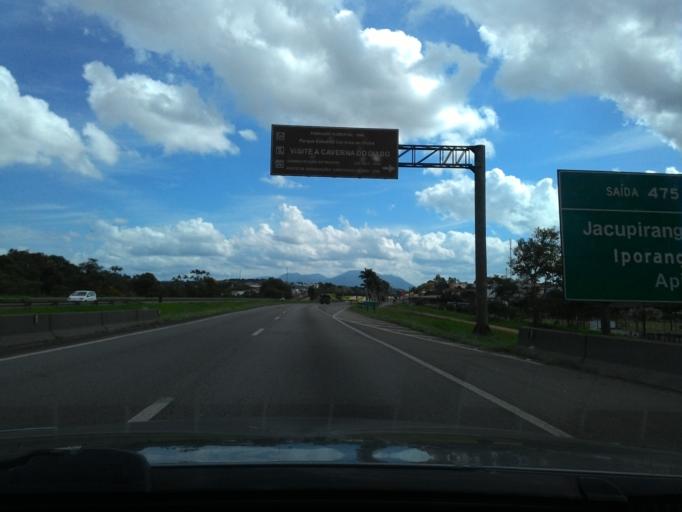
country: BR
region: Sao Paulo
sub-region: Jacupiranga
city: Jacupiranga
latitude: -24.6932
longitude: -47.9965
